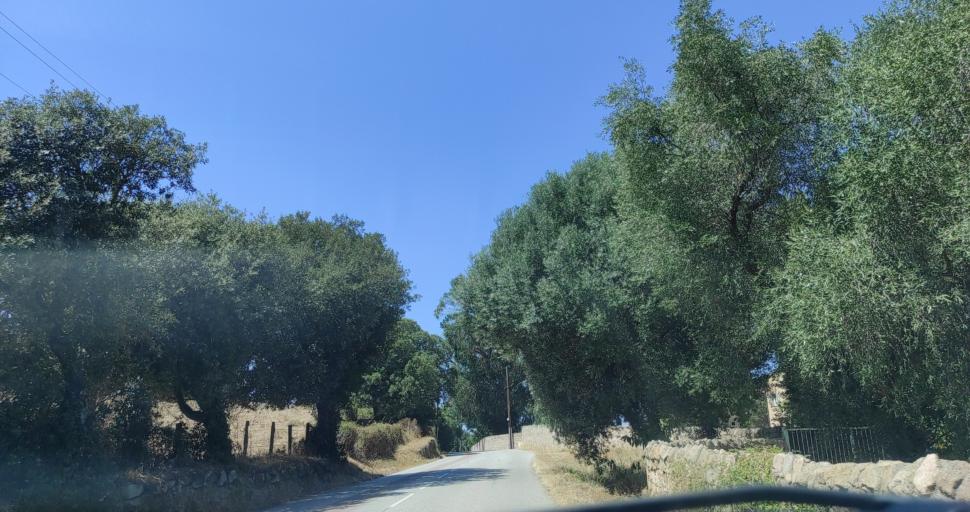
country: FR
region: Corsica
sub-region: Departement de la Corse-du-Sud
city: Alata
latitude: 41.9642
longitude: 8.7212
